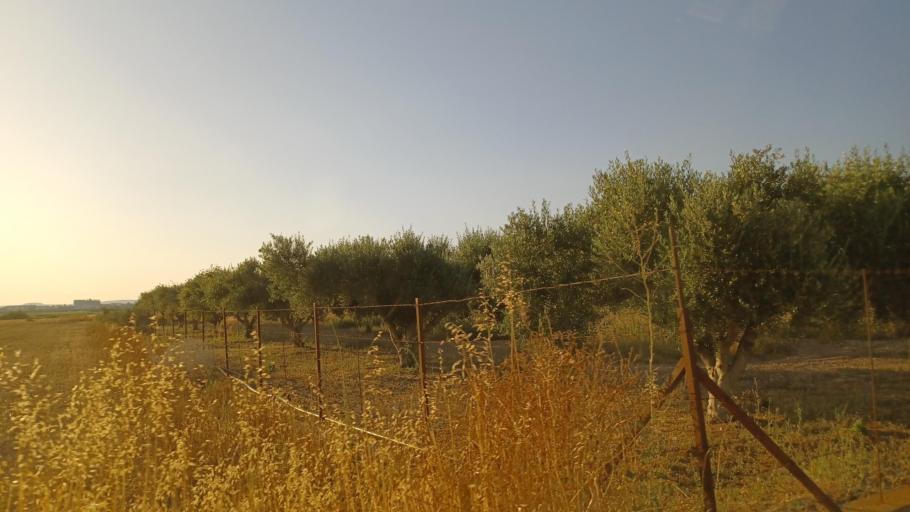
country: CY
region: Larnaka
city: Athienou
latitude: 35.0567
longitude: 33.4988
